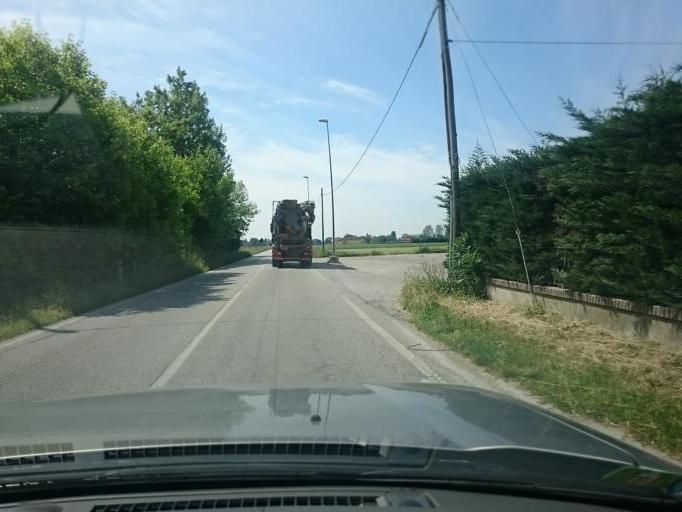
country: IT
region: Veneto
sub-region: Provincia di Padova
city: Monselice
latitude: 45.2137
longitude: 11.7357
